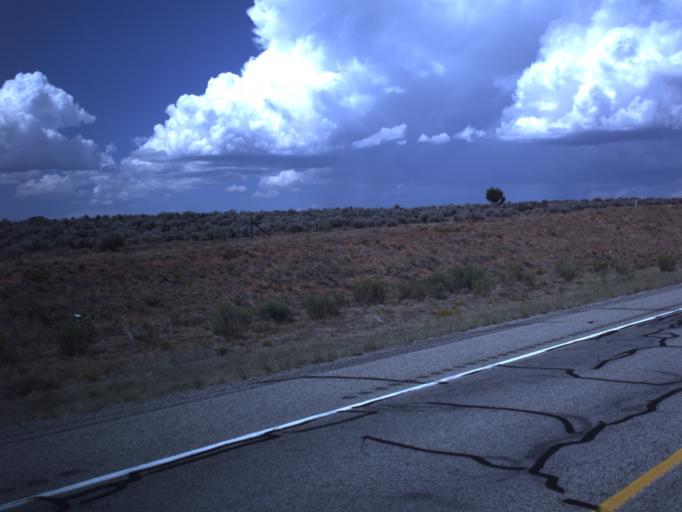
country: US
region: Utah
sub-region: San Juan County
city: Blanding
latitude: 37.5000
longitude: -109.4852
